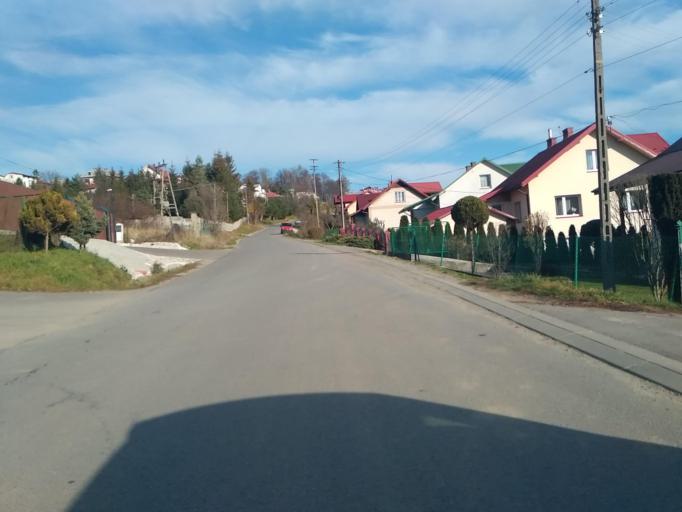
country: PL
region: Subcarpathian Voivodeship
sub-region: Powiat brzozowski
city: Brzozow
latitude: 49.6894
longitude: 22.0083
